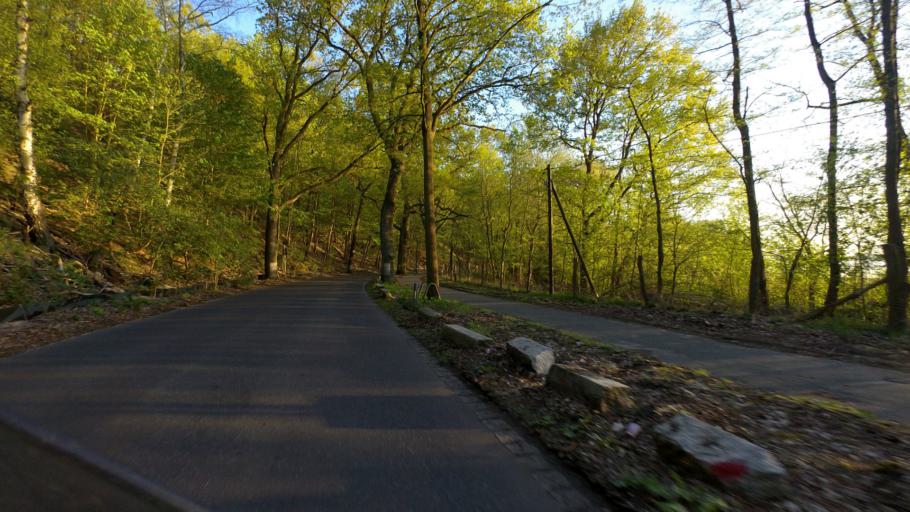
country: DE
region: Berlin
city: Gatow
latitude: 52.4665
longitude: 13.1966
